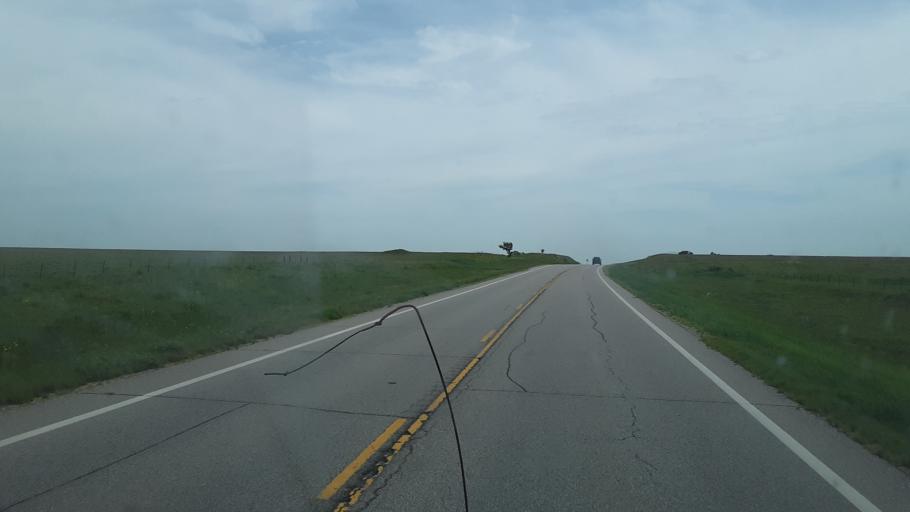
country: US
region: Kansas
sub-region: Greenwood County
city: Eureka
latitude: 37.8102
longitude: -96.5515
